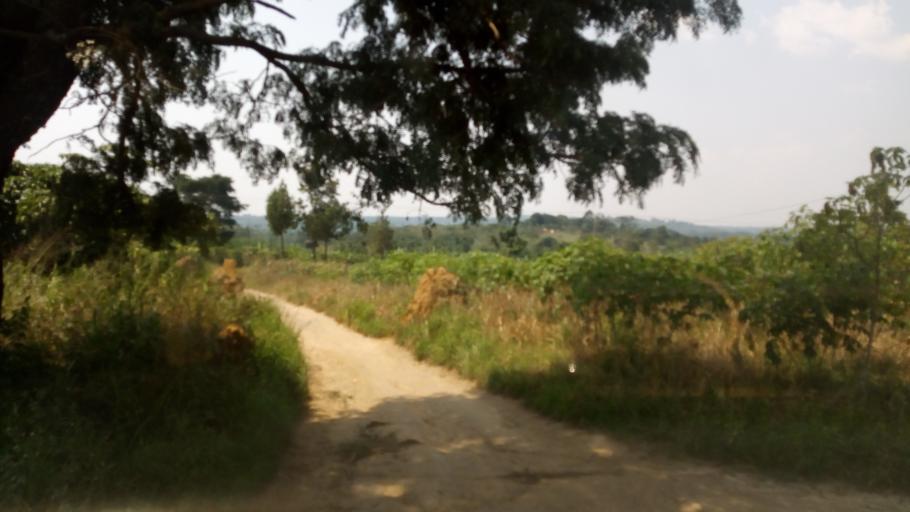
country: UG
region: Western Region
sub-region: Kanungu District
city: Ntungamo
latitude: -0.8035
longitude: 29.6502
